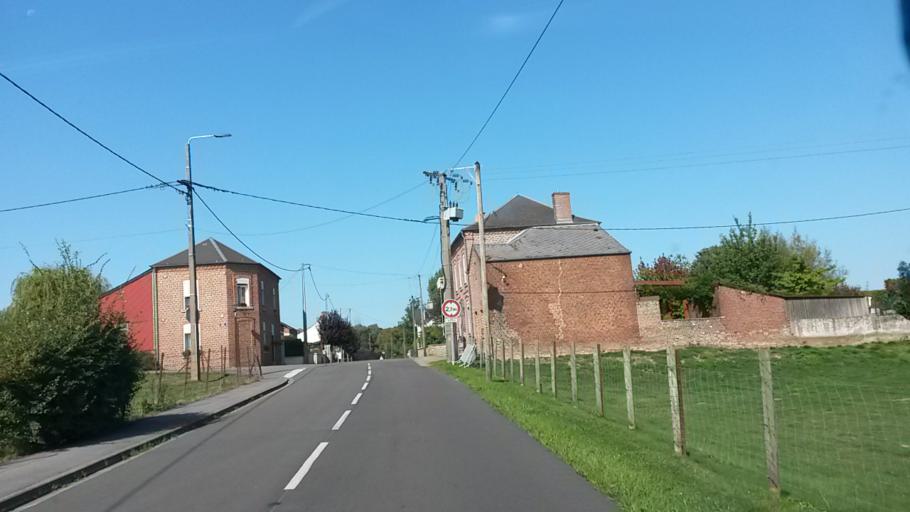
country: FR
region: Nord-Pas-de-Calais
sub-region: Departement du Nord
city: Avesnelles
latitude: 50.1223
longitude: 3.9430
